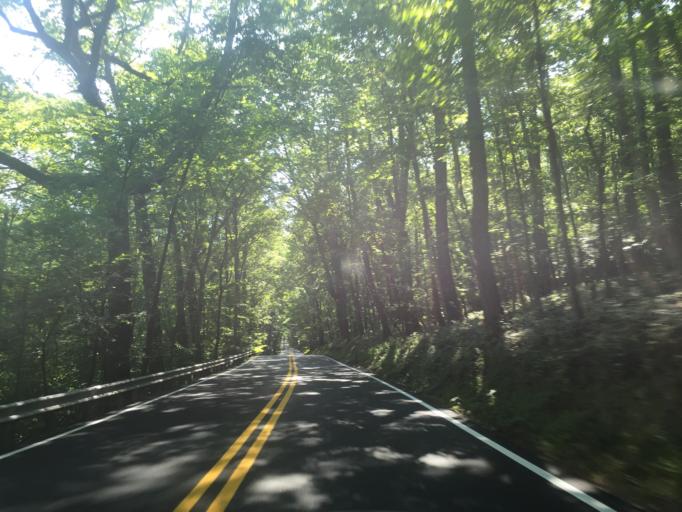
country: US
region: Maryland
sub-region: Baltimore County
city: Mays Chapel
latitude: 39.4131
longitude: -76.6833
